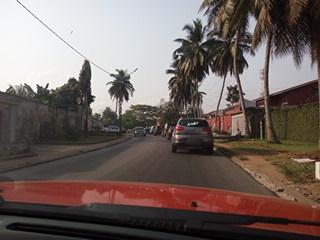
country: CI
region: Lagunes
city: Abobo
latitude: 5.3679
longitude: -3.9918
